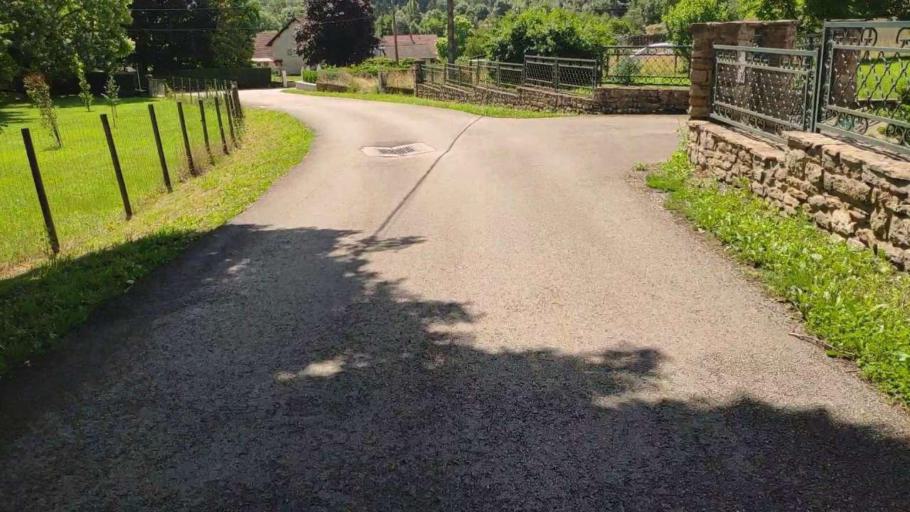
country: FR
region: Franche-Comte
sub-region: Departement du Jura
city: Bletterans
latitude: 46.8305
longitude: 5.5586
